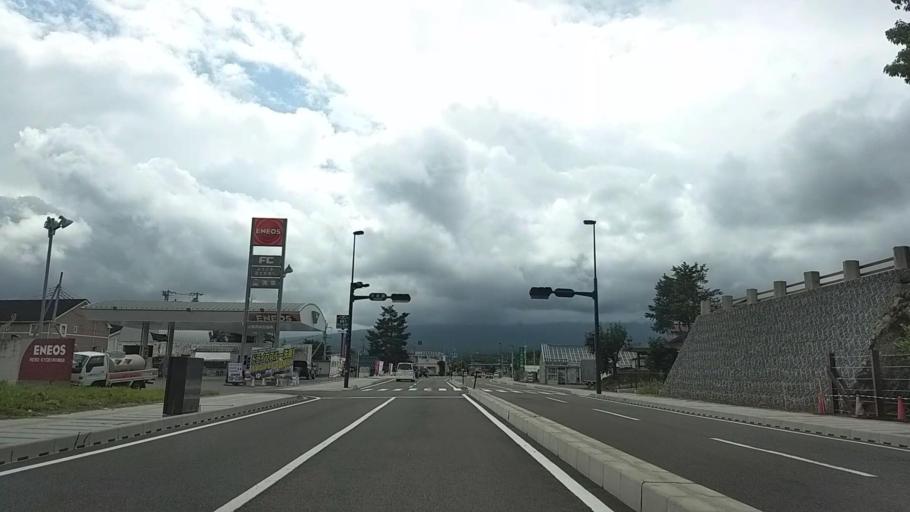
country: JP
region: Yamanashi
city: Fujikawaguchiko
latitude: 35.4947
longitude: 138.7564
